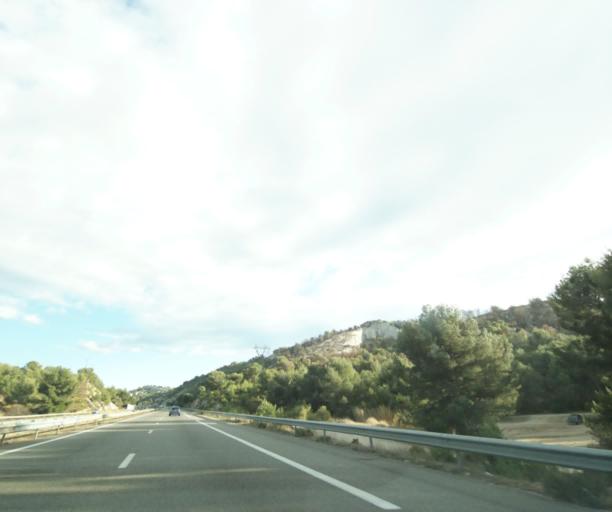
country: FR
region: Provence-Alpes-Cote d'Azur
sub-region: Departement des Bouches-du-Rhone
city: Chateauneuf-les-Martigues
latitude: 43.3854
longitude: 5.1496
